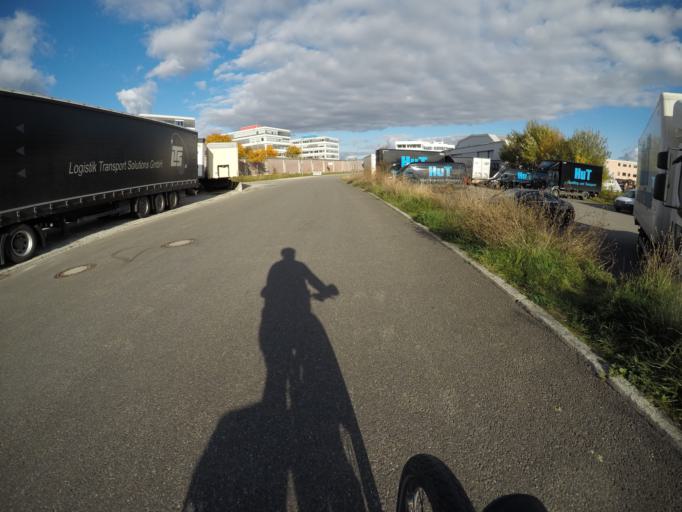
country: DE
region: Baden-Wuerttemberg
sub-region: Regierungsbezirk Stuttgart
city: Filderstadt
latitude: 48.6814
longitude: 9.2072
